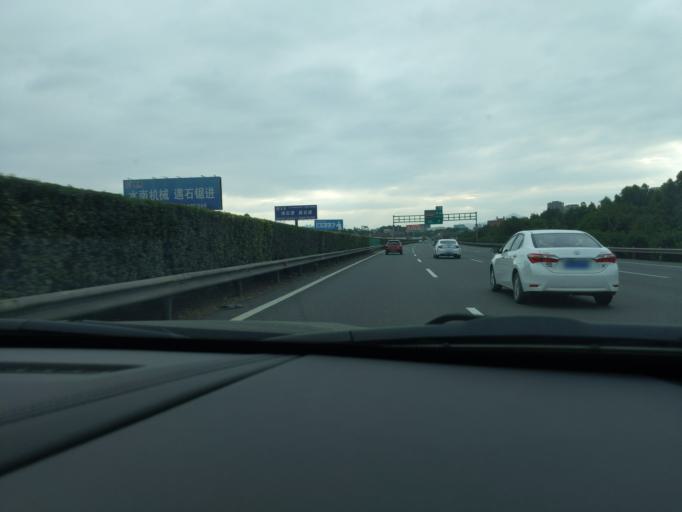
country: CN
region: Fujian
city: Anhai
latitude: 24.7359
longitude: 118.4215
